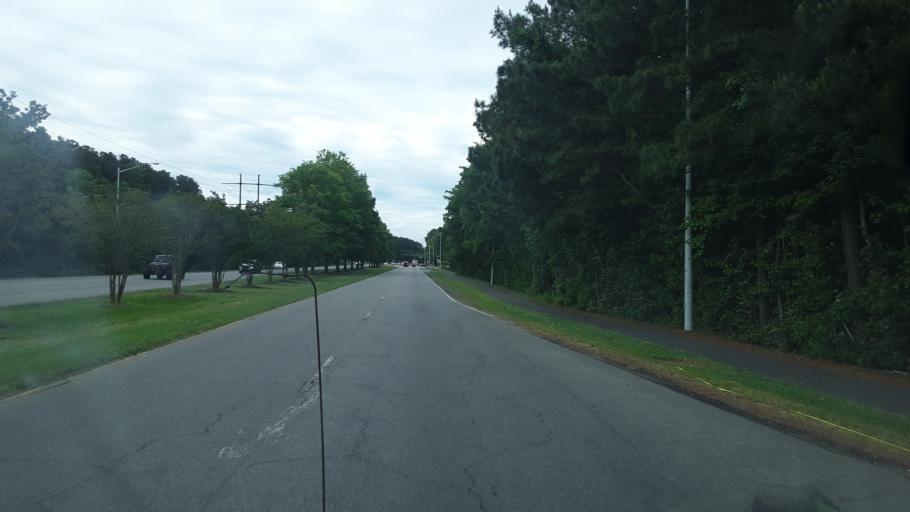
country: US
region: Virginia
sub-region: City of Virginia Beach
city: Virginia Beach
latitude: 36.7974
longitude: -75.9944
